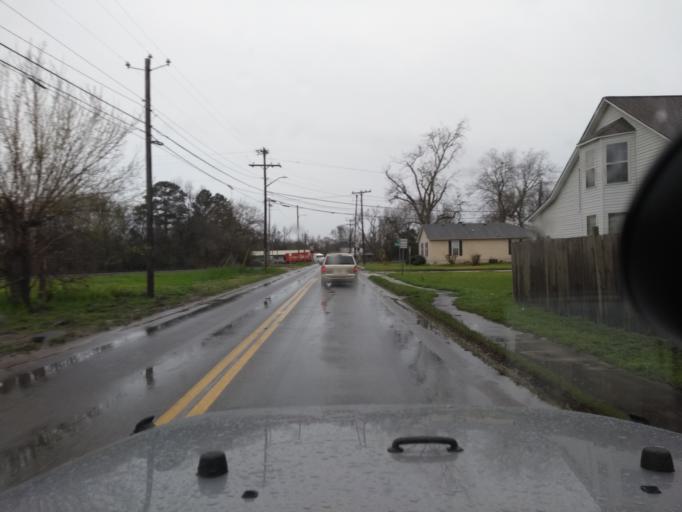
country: US
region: Georgia
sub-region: Chatham County
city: Garden City
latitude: 32.0880
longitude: -81.1394
